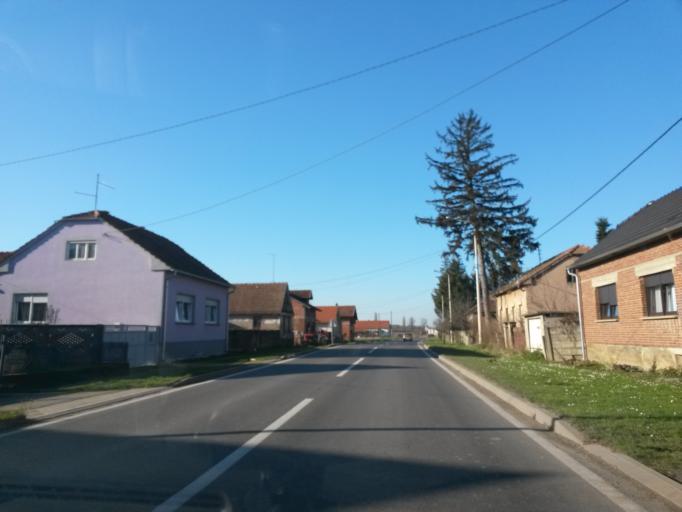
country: HR
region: Koprivnicko-Krizevacka
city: Virje
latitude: 46.0879
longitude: 16.9464
